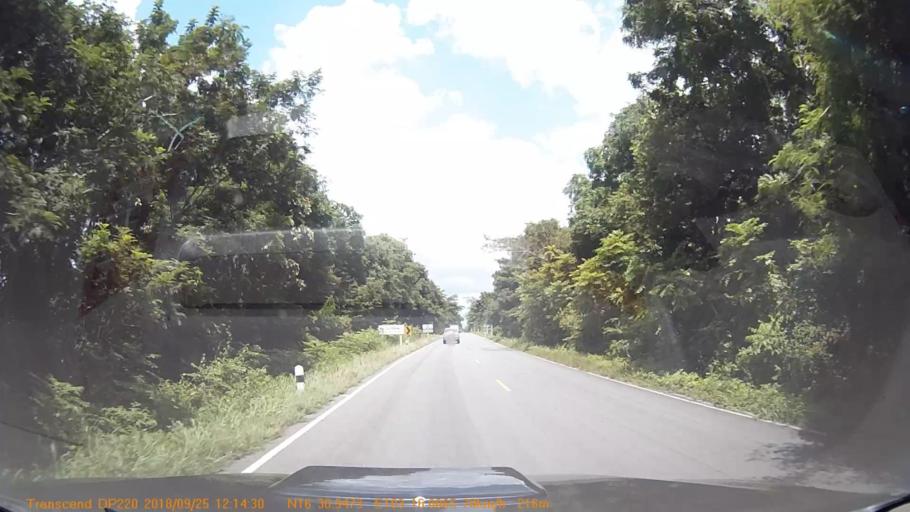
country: TH
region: Kalasin
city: Huai Mek
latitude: 16.5158
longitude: 103.2668
